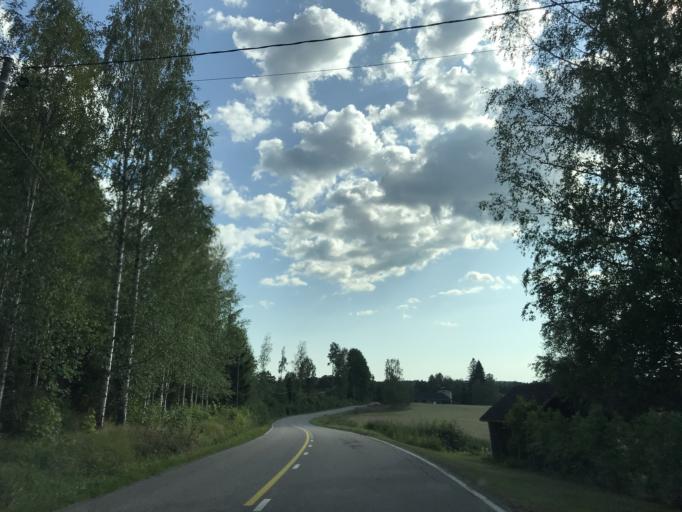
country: FI
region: Uusimaa
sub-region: Helsinki
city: Vihti
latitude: 60.4351
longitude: 24.5396
